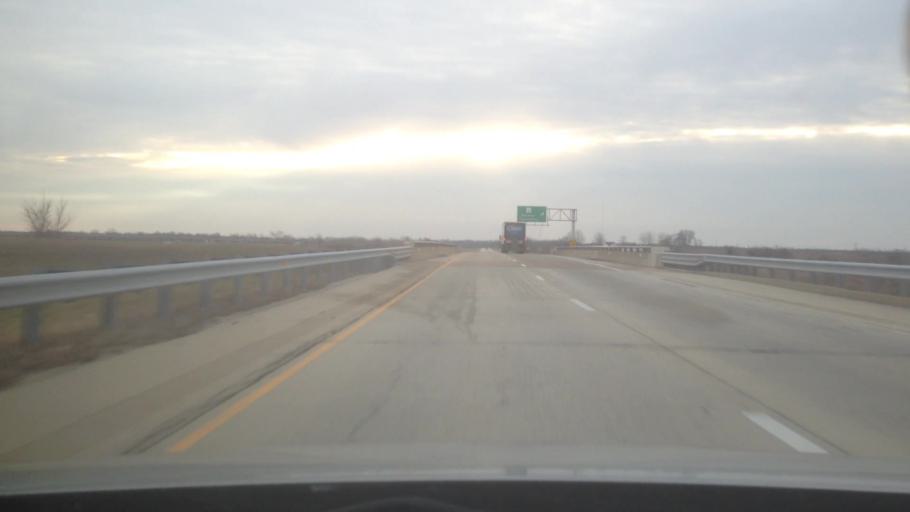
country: US
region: Illinois
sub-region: Macon County
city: Decatur
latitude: 39.8005
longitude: -89.0091
